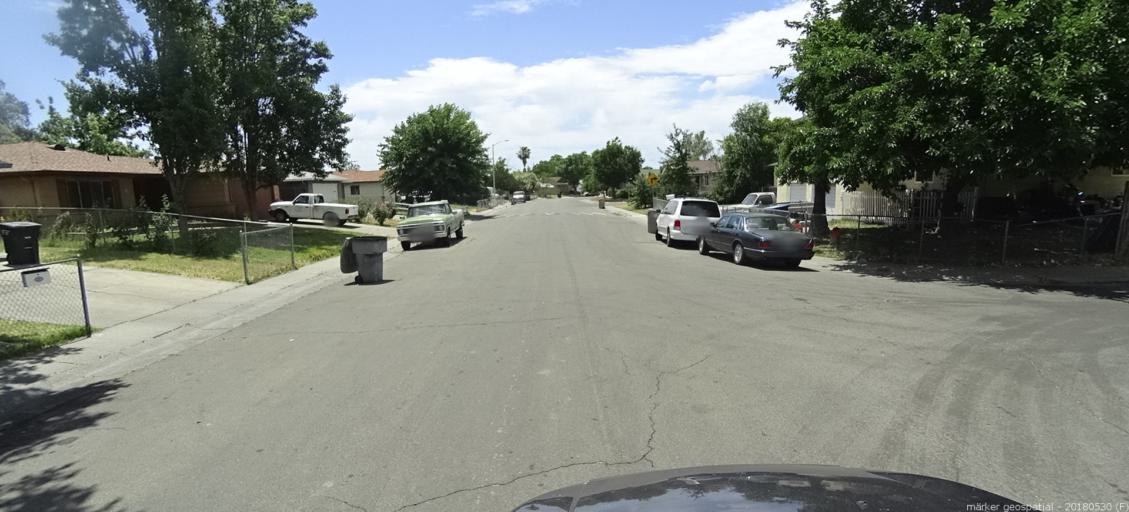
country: US
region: California
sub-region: Sacramento County
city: Sacramento
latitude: 38.6225
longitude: -121.4652
